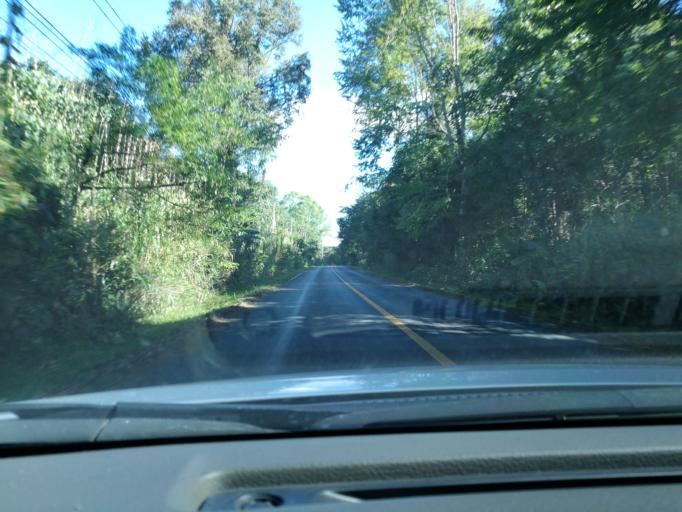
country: TH
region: Phitsanulok
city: Nakhon Thai
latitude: 16.9961
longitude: 101.0036
